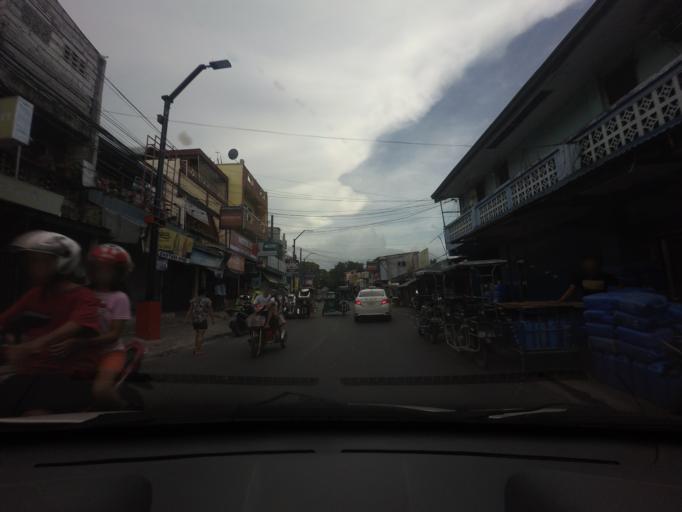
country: PH
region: Calabarzon
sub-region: Province of Rizal
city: Taguig
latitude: 14.5060
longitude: 121.0537
